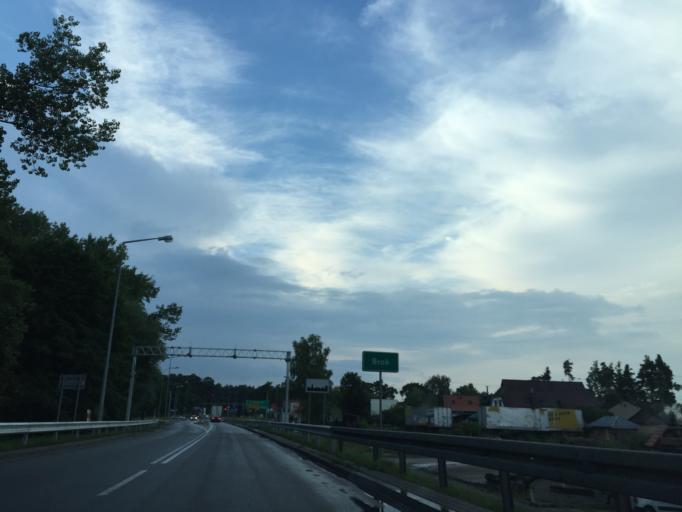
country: PL
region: Masovian Voivodeship
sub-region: Powiat ostrowski
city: Brok
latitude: 52.6958
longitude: 21.8485
